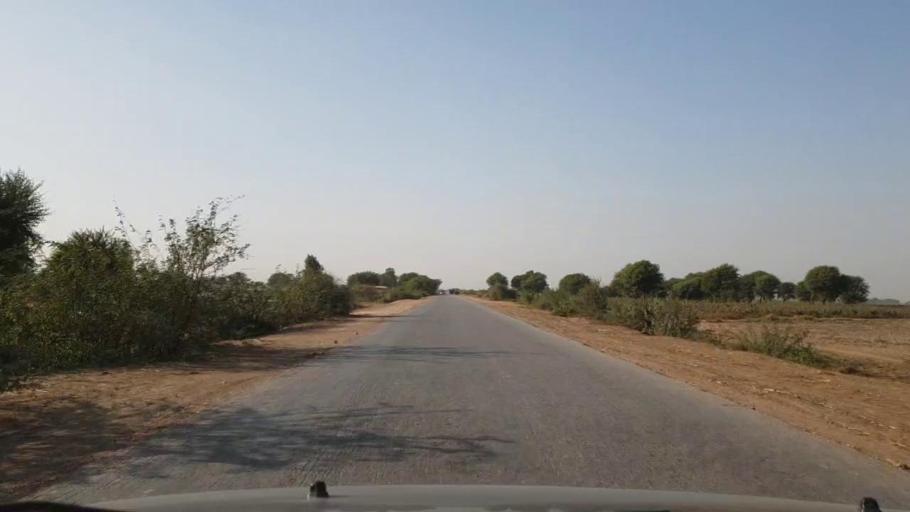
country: PK
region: Sindh
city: Tando Ghulam Ali
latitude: 25.1775
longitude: 68.8266
